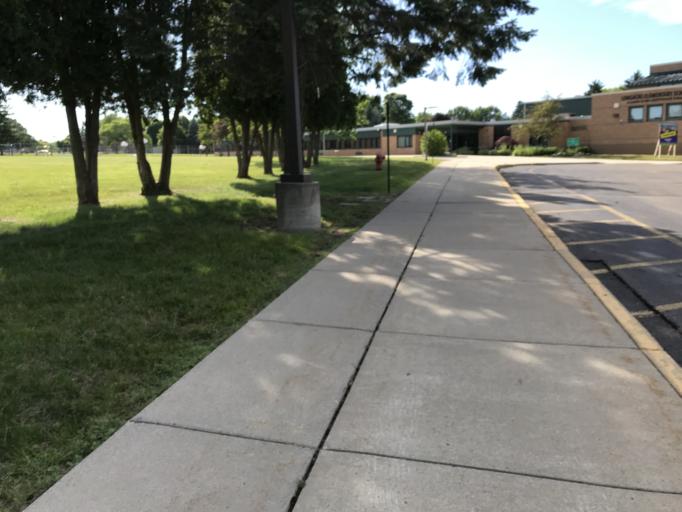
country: US
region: Michigan
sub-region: Oakland County
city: Farmington
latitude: 42.4628
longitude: -83.3917
